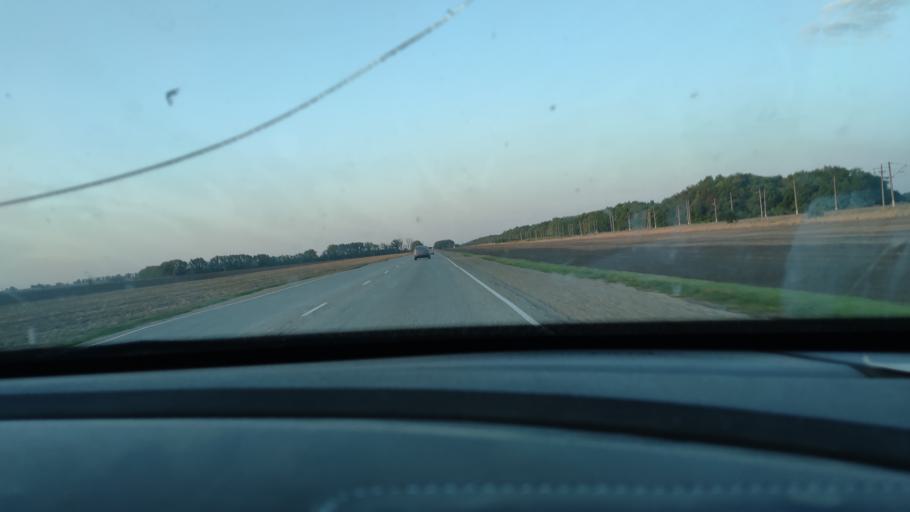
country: RU
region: Krasnodarskiy
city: Starominskaya
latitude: 46.4681
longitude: 39.0424
